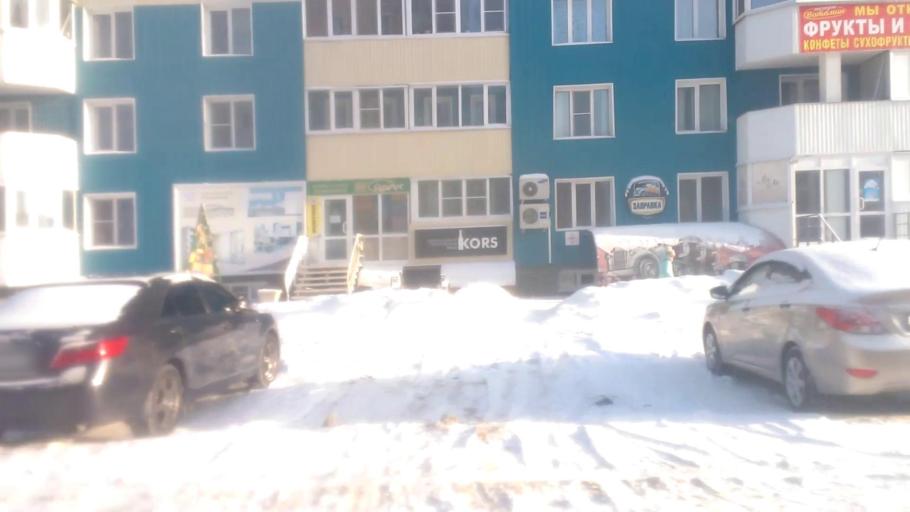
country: RU
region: Altai Krai
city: Novosilikatnyy
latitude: 53.3417
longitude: 83.6550
